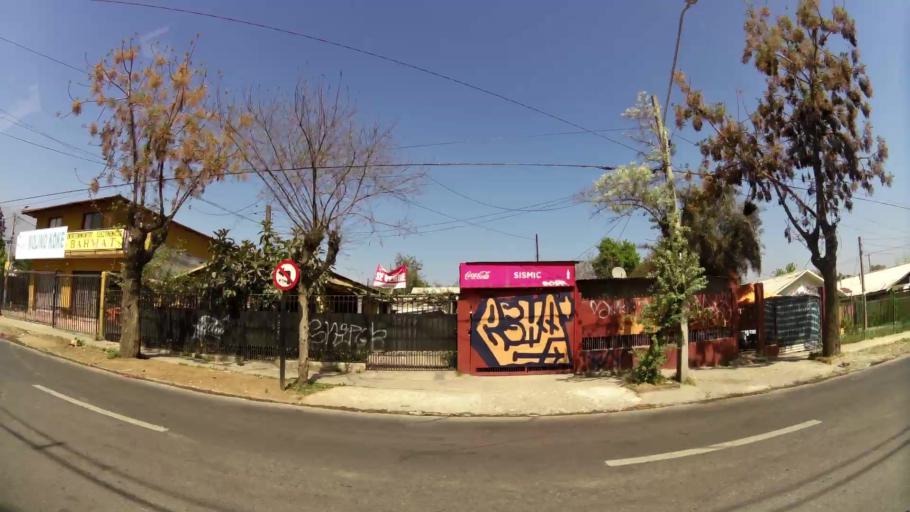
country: CL
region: Santiago Metropolitan
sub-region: Provincia de Santiago
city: Villa Presidente Frei, Nunoa, Santiago, Chile
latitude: -33.4703
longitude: -70.5489
